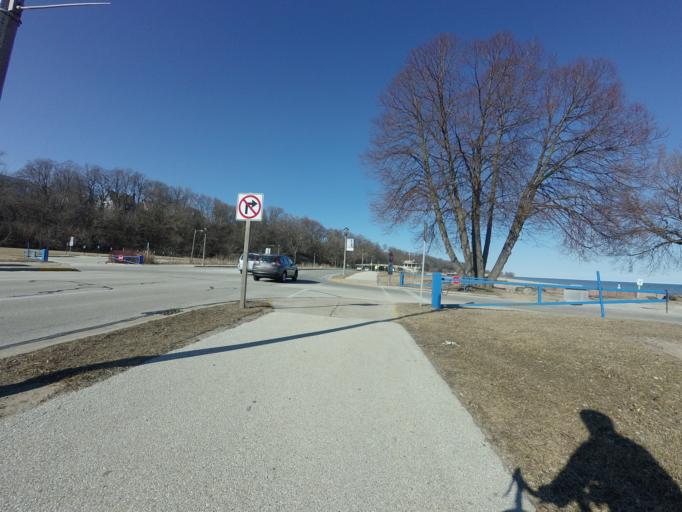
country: US
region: Wisconsin
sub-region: Milwaukee County
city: Shorewood
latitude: 43.0591
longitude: -87.8763
